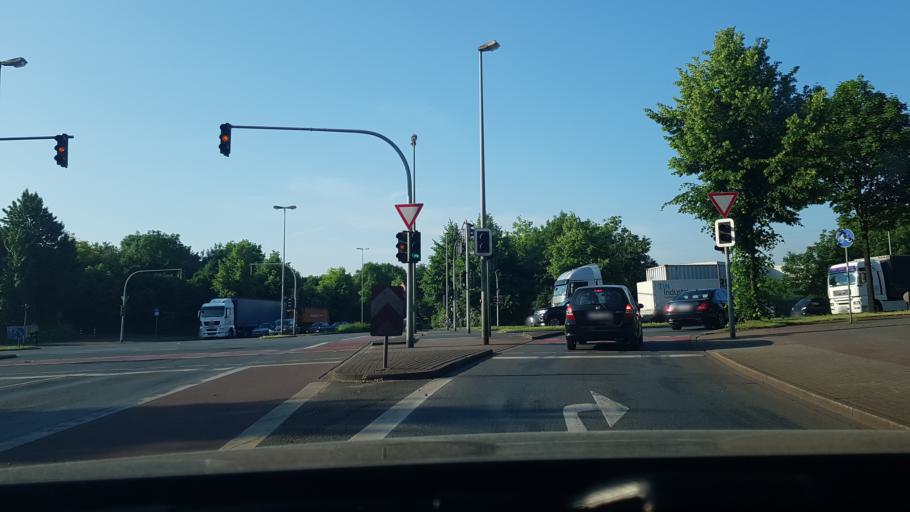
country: DE
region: North Rhine-Westphalia
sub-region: Regierungsbezirk Dusseldorf
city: Hochfeld
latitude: 51.4203
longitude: 6.7468
